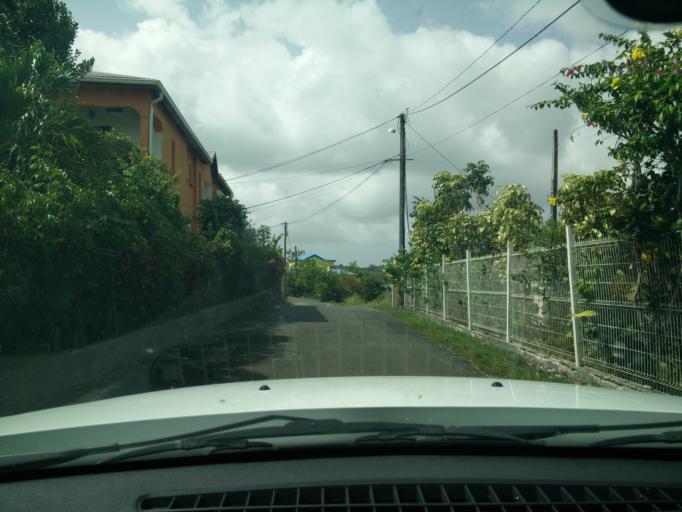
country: GP
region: Guadeloupe
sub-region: Guadeloupe
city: Sainte-Anne
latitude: 16.2147
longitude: -61.4328
